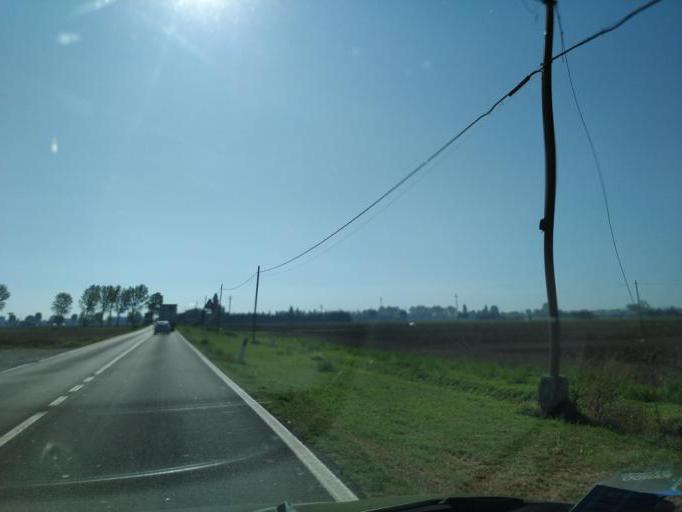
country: IT
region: Emilia-Romagna
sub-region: Provincia di Bologna
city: Sant'Agata Bolognese
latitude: 44.6658
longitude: 11.1065
